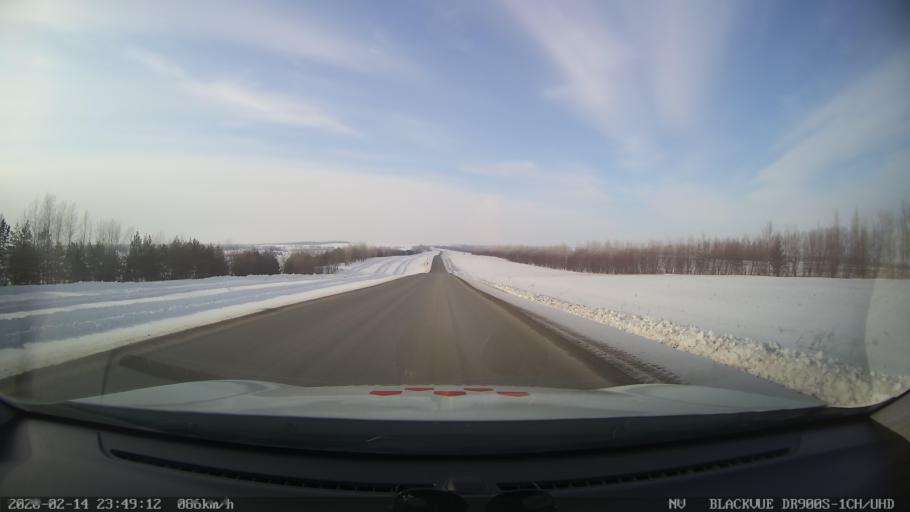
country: RU
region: Tatarstan
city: Kuybyshevskiy Zaton
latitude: 55.2519
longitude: 49.1879
